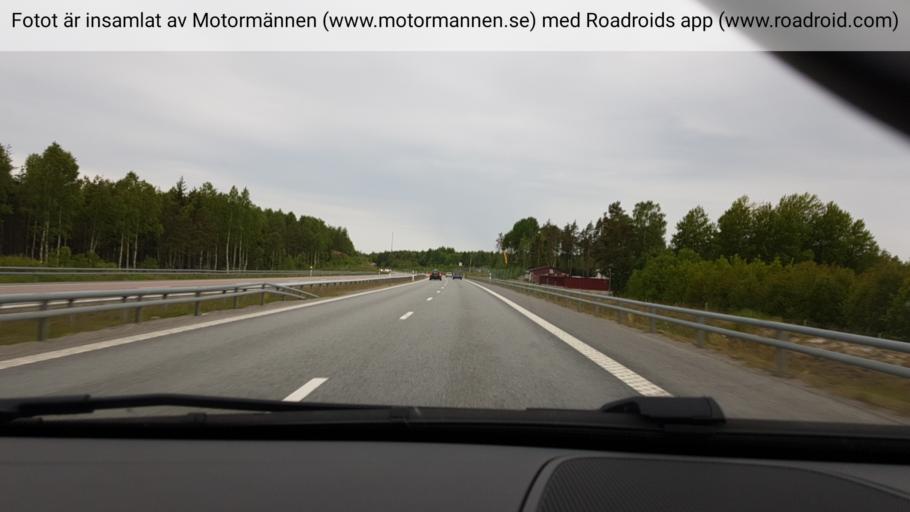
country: SE
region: Stockholm
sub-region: Haninge Kommun
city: Jordbro
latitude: 59.0879
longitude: 18.0861
